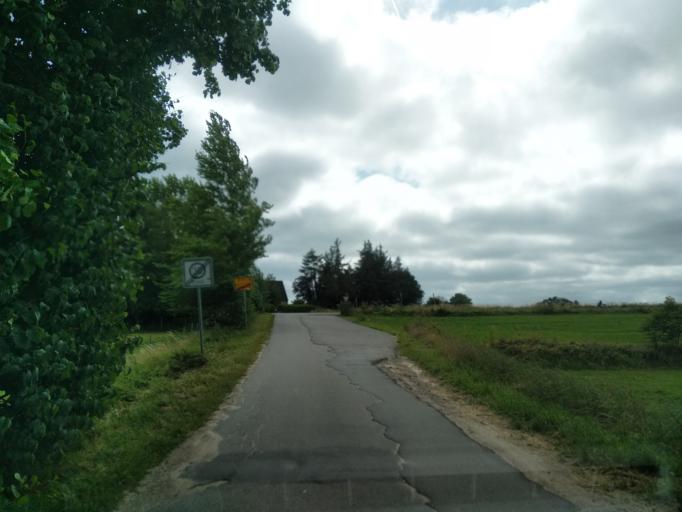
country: DE
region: Schleswig-Holstein
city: Langballig
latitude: 54.7987
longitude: 9.6299
